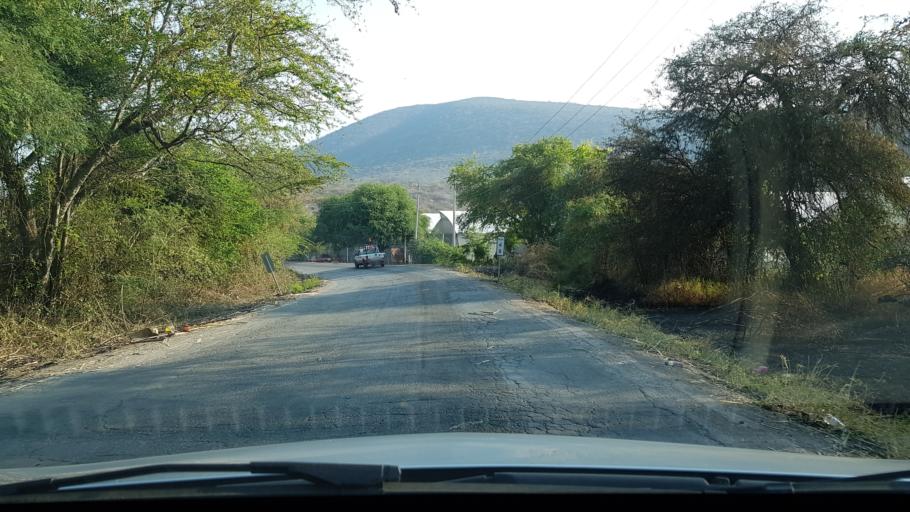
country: MX
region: Morelos
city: Tlaltizapan
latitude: 18.6827
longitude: -99.0890
